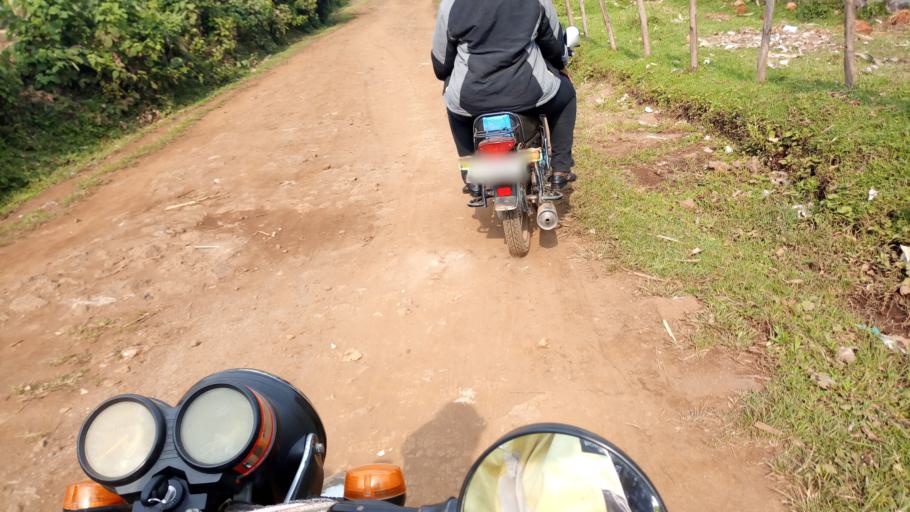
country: UG
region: Western Region
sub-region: Kisoro District
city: Kisoro
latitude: -1.3102
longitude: 29.6572
